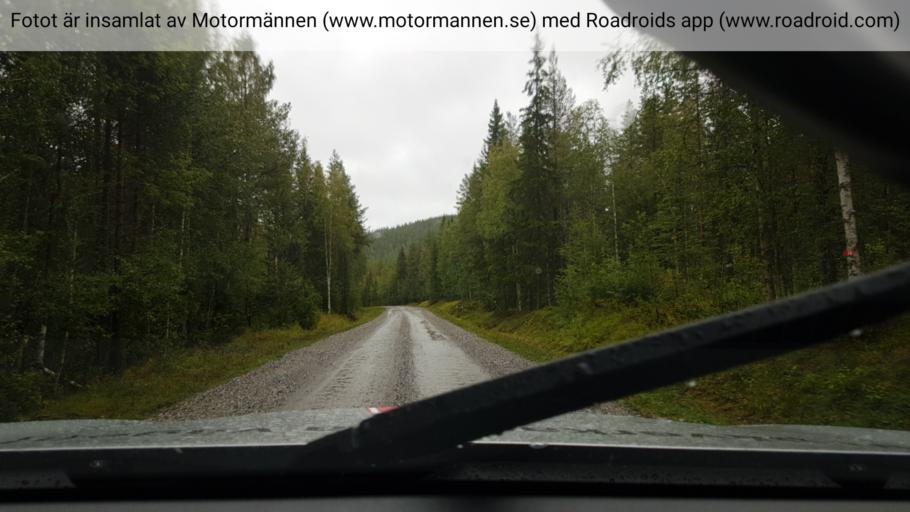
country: SE
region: Vaesterbotten
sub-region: Asele Kommun
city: Asele
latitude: 63.9948
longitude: 17.6028
